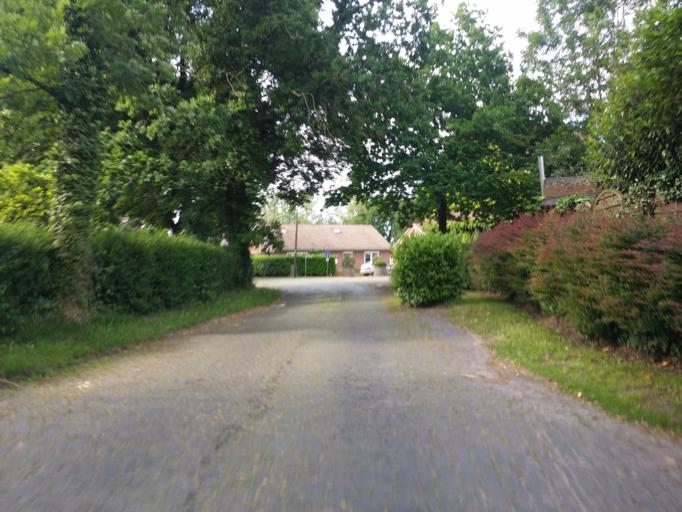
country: DE
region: Lower Saxony
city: Bockhorn
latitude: 53.3685
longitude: 7.9951
